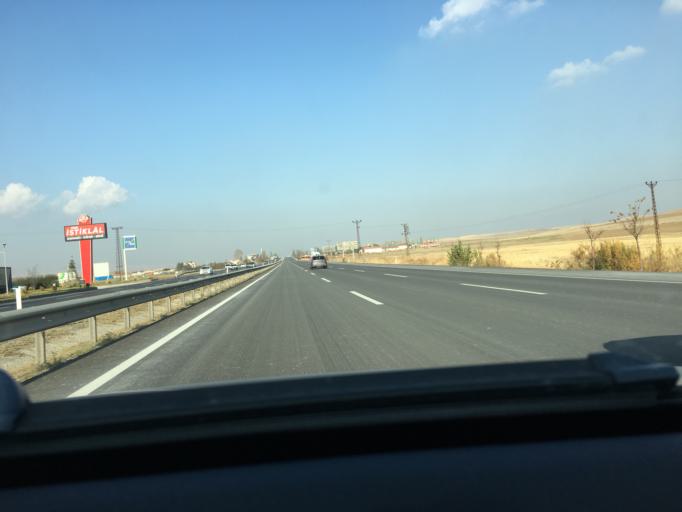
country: TR
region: Ankara
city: Polatli
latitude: 39.6593
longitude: 32.2211
